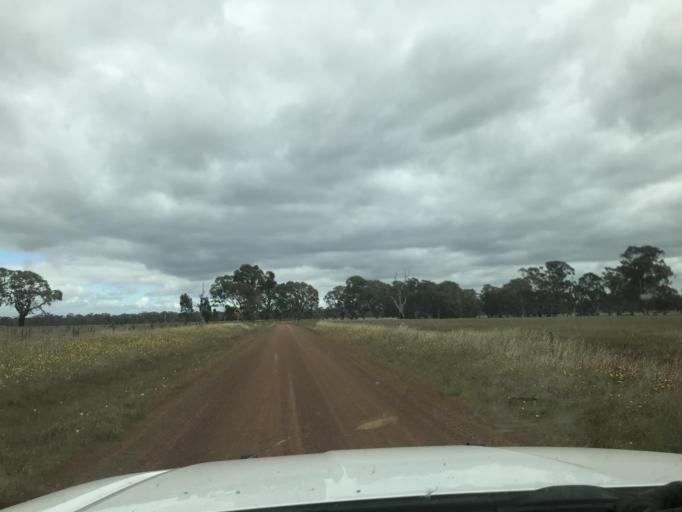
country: AU
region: South Australia
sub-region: Wattle Range
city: Penola
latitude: -37.1020
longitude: 141.2329
